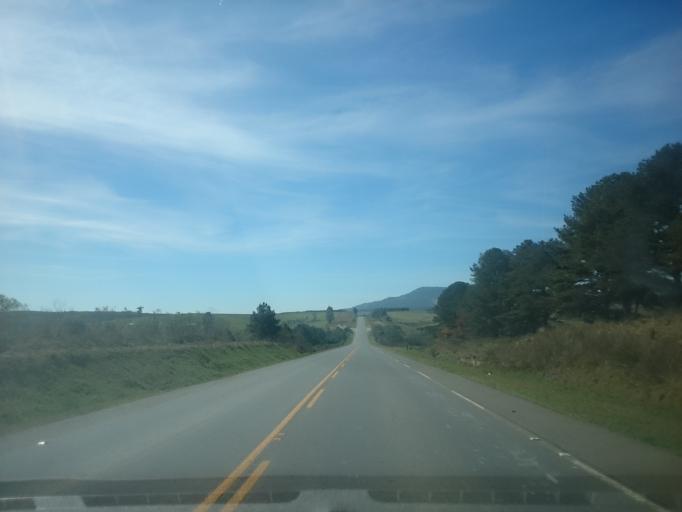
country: BR
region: Santa Catarina
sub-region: Lages
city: Lages
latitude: -27.7693
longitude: -50.1760
